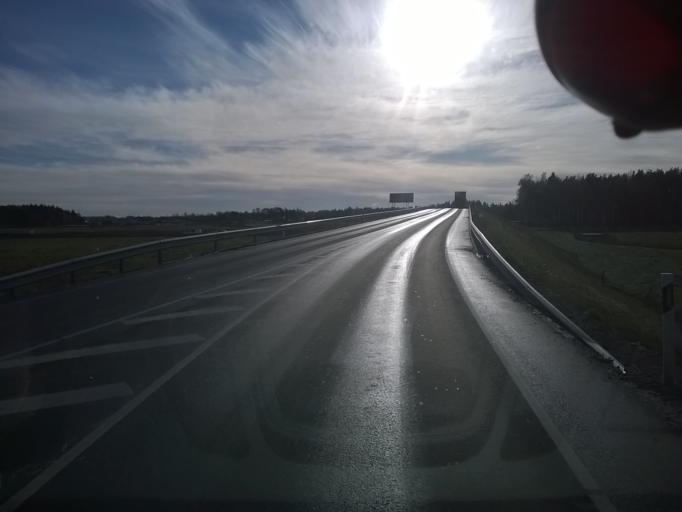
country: EE
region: Harju
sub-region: Saku vald
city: Saku
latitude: 59.3171
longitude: 24.6419
